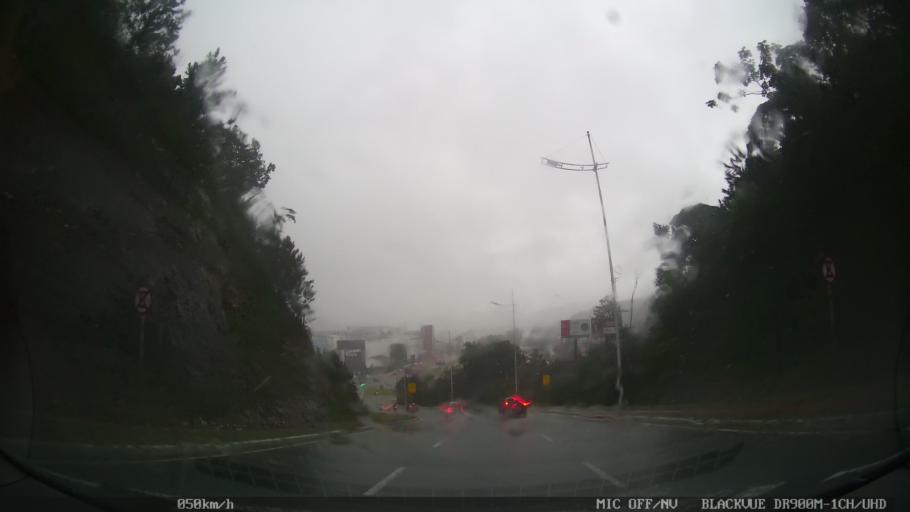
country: BR
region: Santa Catarina
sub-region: Balneario Camboriu
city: Balneario Camboriu
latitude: -26.9904
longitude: -48.6453
